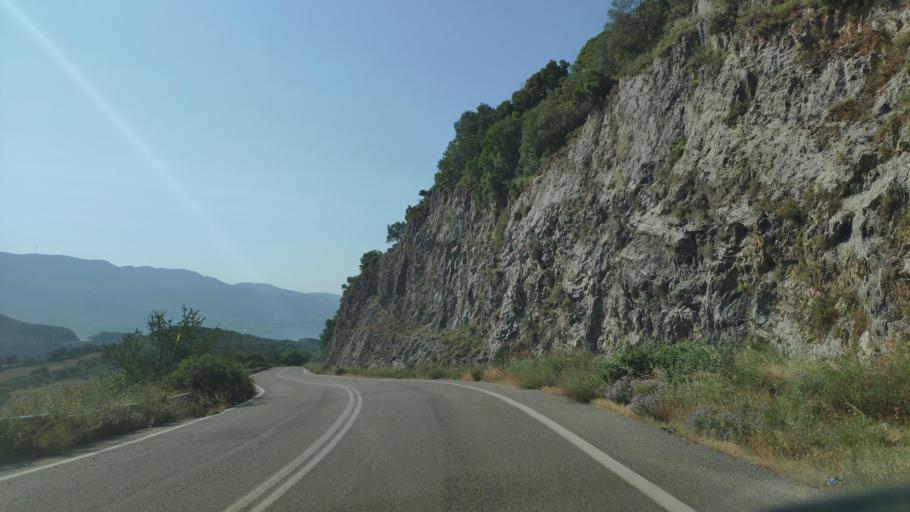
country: GR
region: West Greece
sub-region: Nomos Aitolias kai Akarnanias
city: Katouna
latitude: 38.7788
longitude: 21.1364
